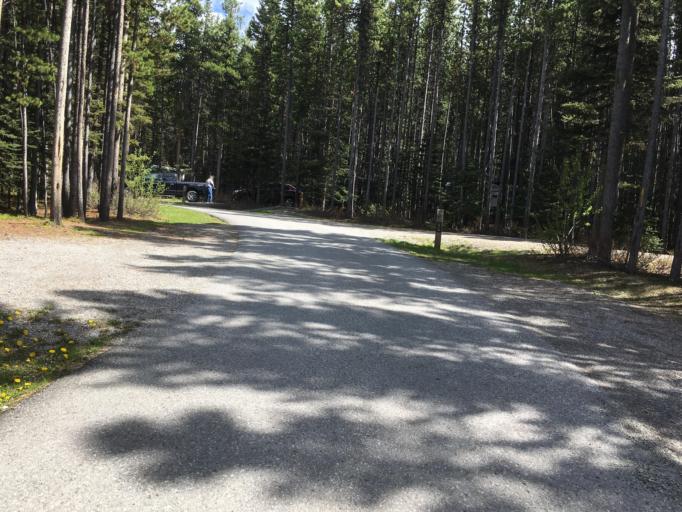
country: CA
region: Alberta
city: Canmore
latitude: 50.6259
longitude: -115.1017
